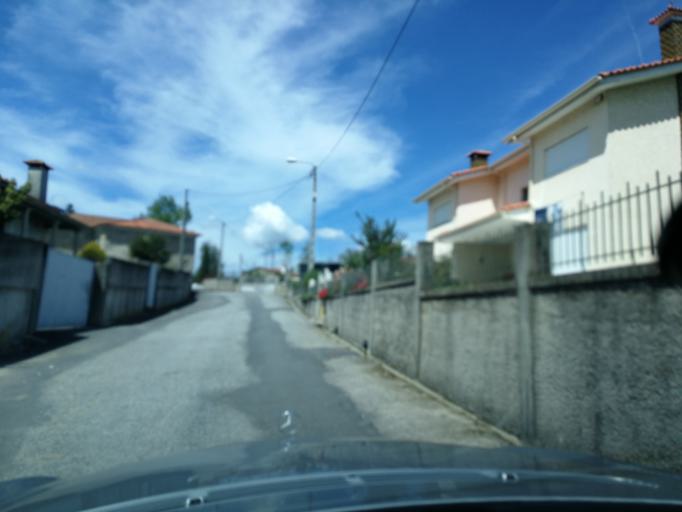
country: PT
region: Braga
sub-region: Vila Nova de Famalicao
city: Vila Nova de Famalicao
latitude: 41.4295
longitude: -8.5273
